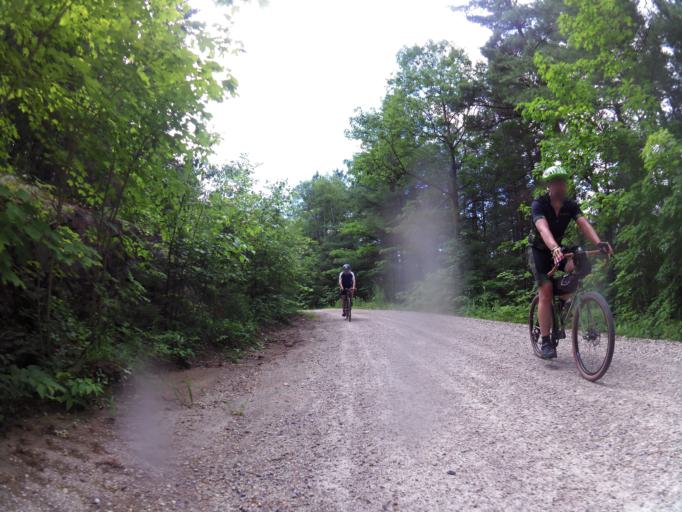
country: CA
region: Ontario
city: Perth
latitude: 45.0159
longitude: -76.5994
